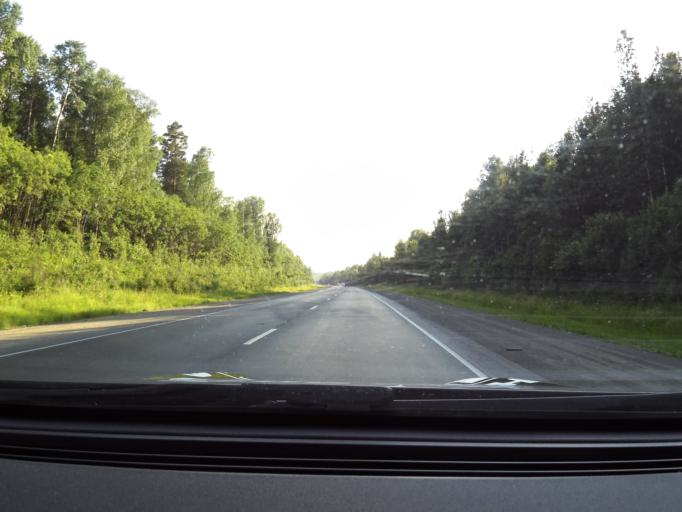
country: RU
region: Sverdlovsk
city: Bilimbay
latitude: 56.8537
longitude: 59.7009
